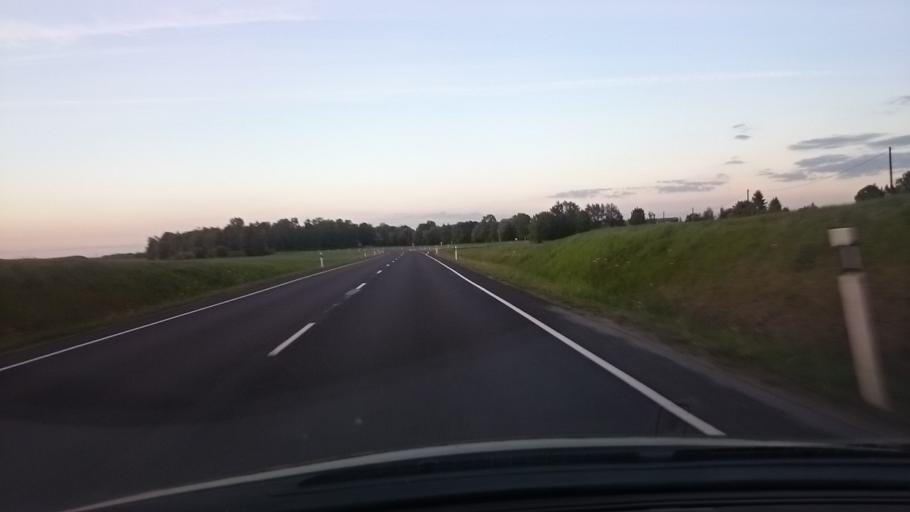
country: EE
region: Viljandimaa
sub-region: Vohma linn
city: Vohma
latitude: 58.6869
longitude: 25.6212
